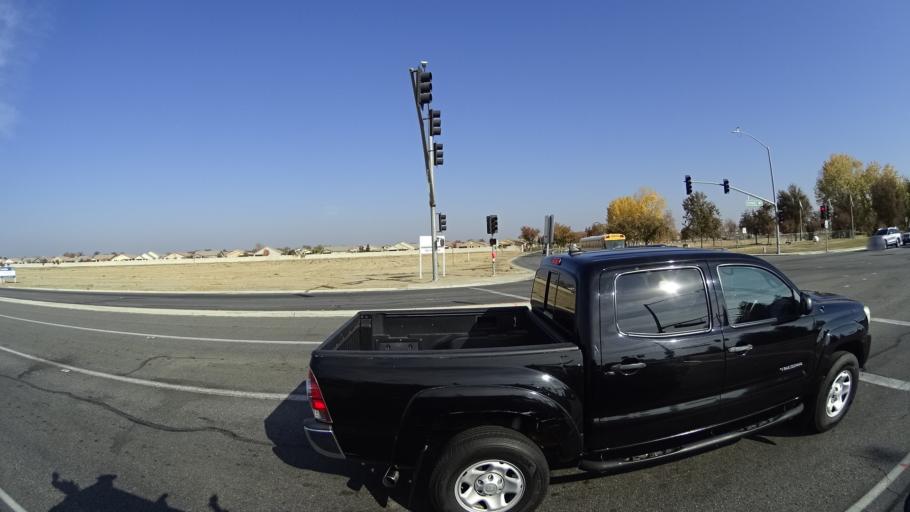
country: US
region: California
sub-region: Kern County
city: Rosedale
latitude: 35.3537
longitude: -119.1371
